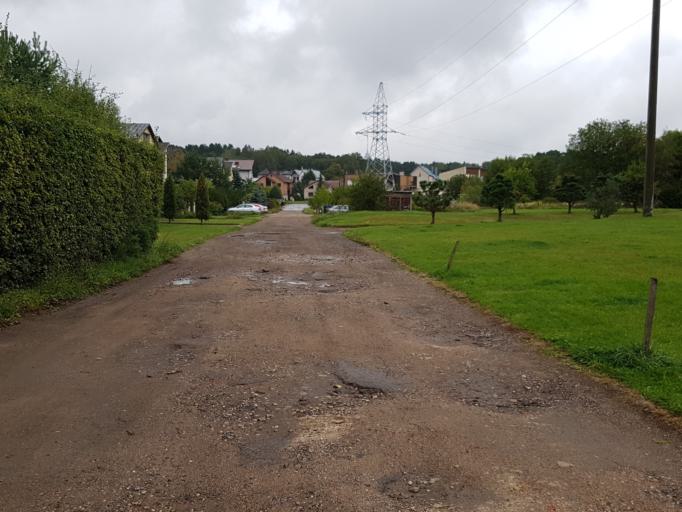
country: LT
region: Vilnius County
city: Lazdynai
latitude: 54.6635
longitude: 25.1863
